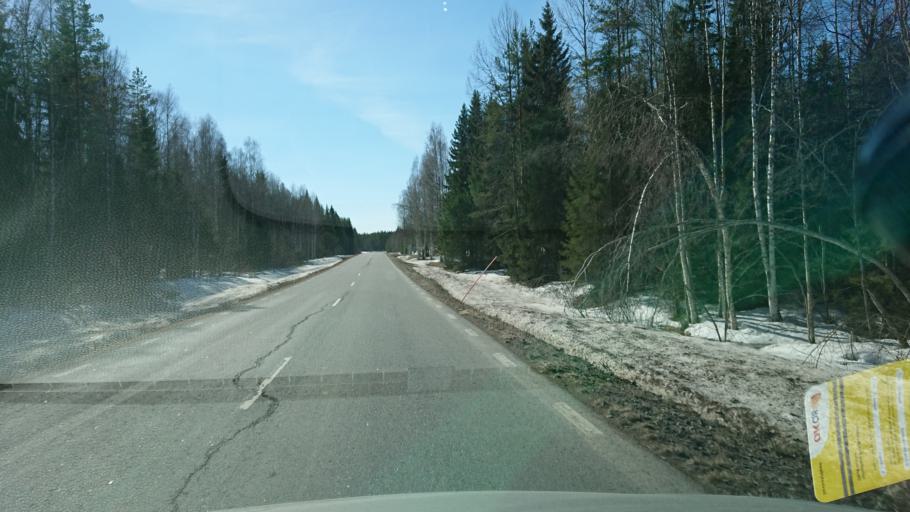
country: SE
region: Vaesternorrland
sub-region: Solleftea Kommun
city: As
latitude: 63.6761
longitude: 16.4321
